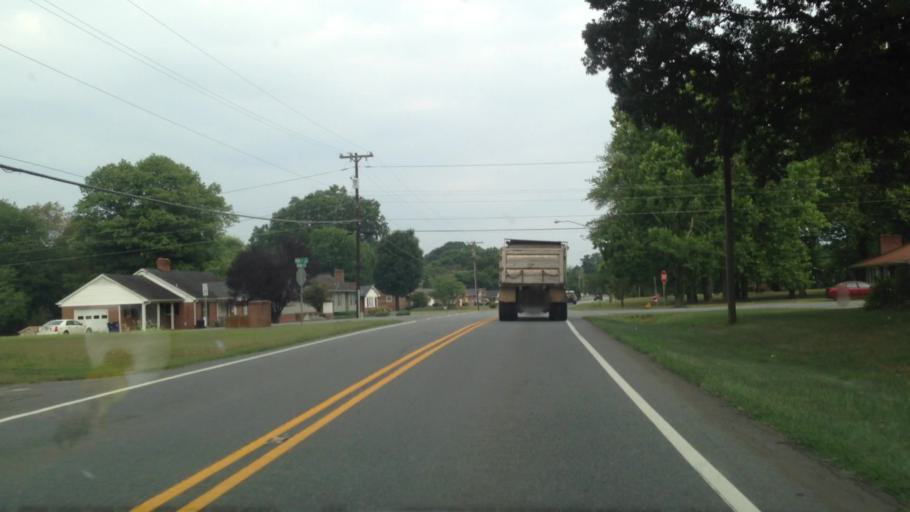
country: US
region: North Carolina
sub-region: Forsyth County
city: Rural Hall
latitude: 36.1980
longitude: -80.2705
